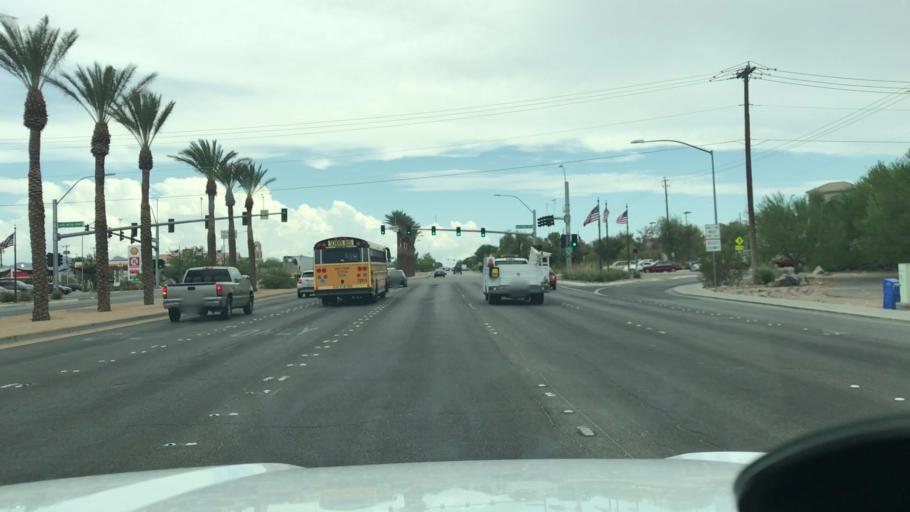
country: US
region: Nevada
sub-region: Clark County
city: Henderson
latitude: 36.0402
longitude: -114.9829
